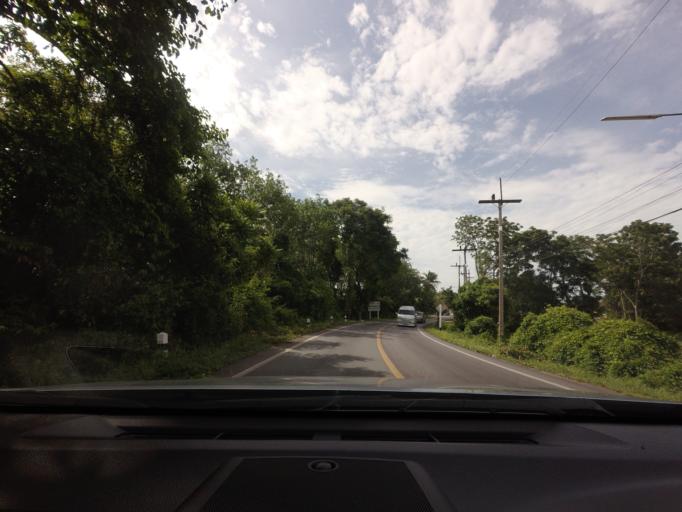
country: TH
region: Songkhla
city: Khlong Hoi Khong
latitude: 6.9089
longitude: 100.4127
